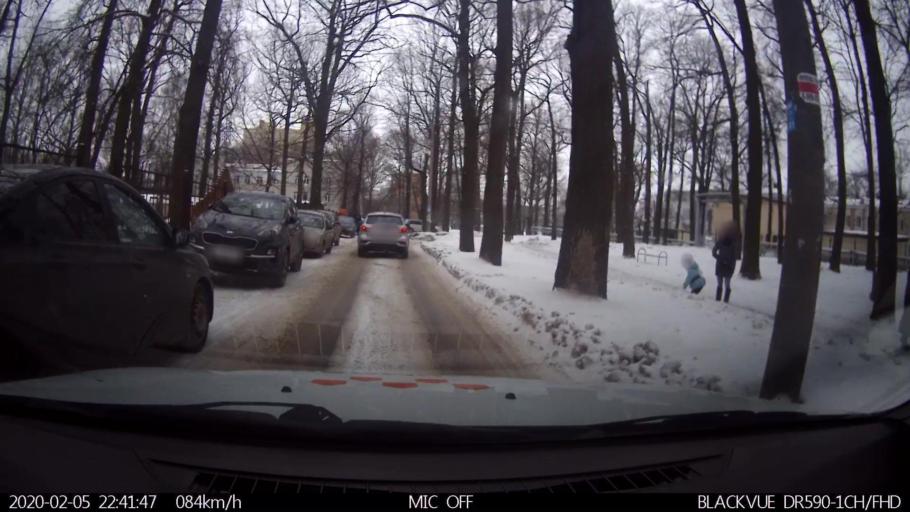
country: RU
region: Nizjnij Novgorod
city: Imeni Stepana Razina
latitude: 54.7199
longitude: 44.3449
